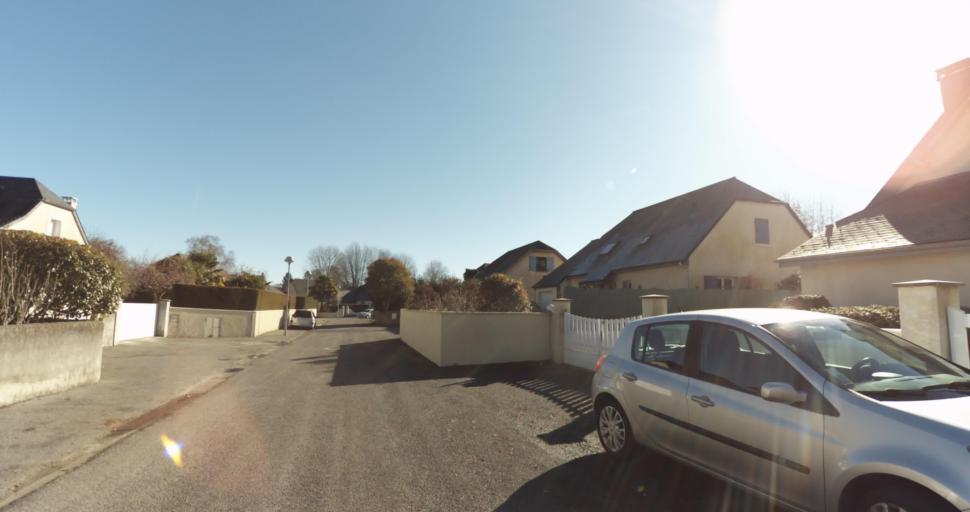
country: FR
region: Aquitaine
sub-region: Departement des Pyrenees-Atlantiques
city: Morlaas
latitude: 43.3456
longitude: -0.2678
